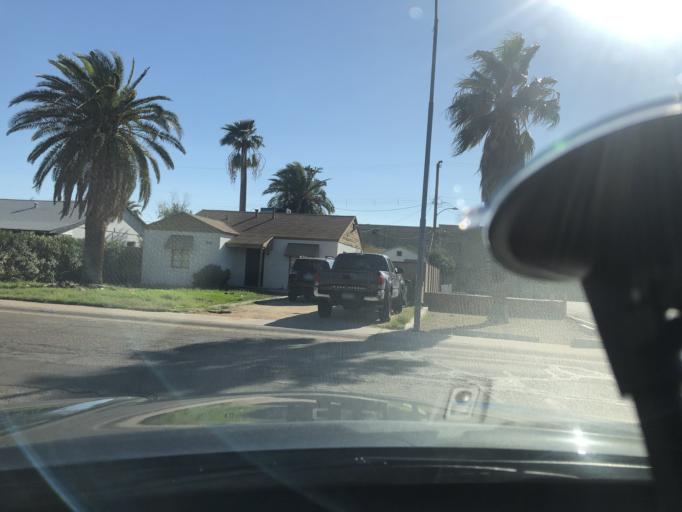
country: US
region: Arizona
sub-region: Maricopa County
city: Phoenix
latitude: 33.4667
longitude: -112.0468
